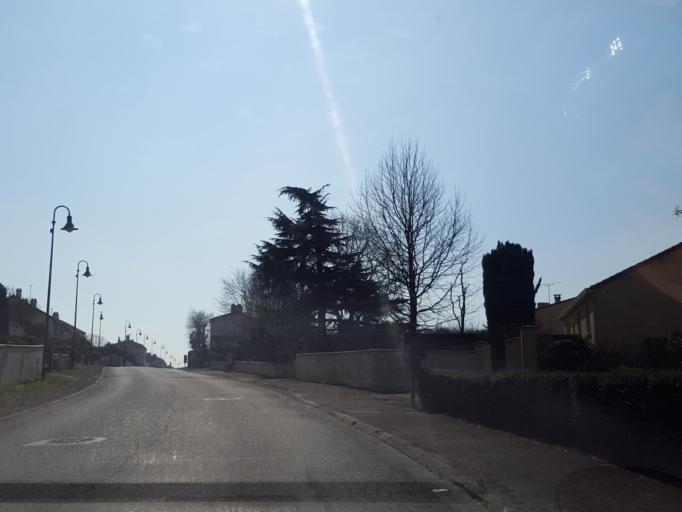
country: FR
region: Pays de la Loire
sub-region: Departement de la Vendee
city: Chavagnes-en-Paillers
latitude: 46.8618
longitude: -1.2624
